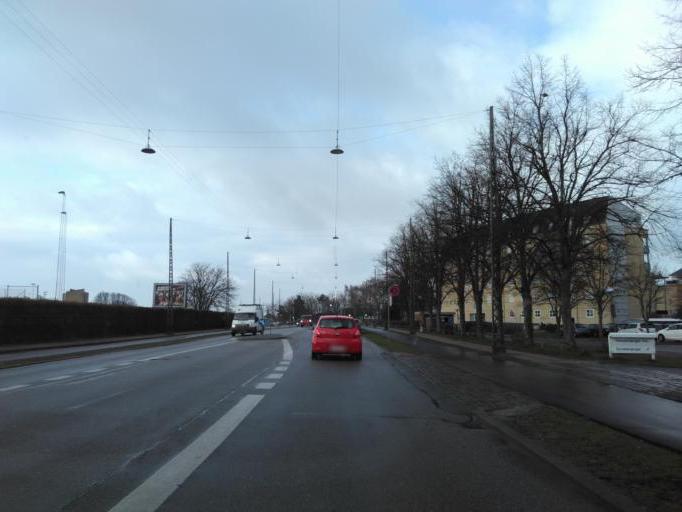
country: DK
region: Capital Region
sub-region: Tarnby Kommune
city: Tarnby
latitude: 55.6498
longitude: 12.5992
